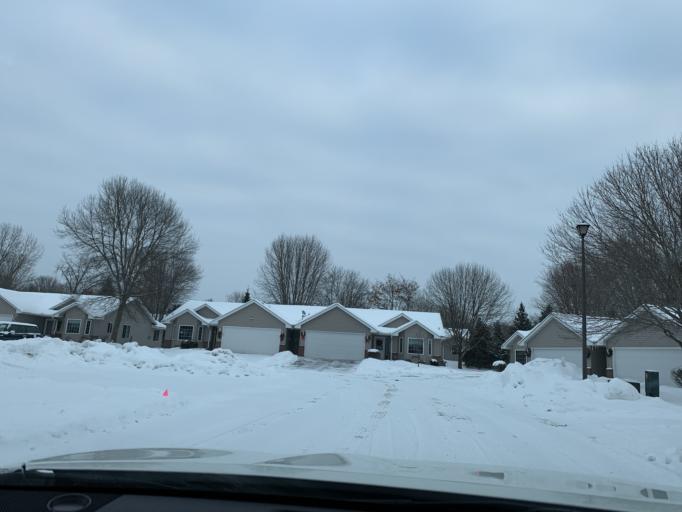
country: US
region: Minnesota
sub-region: Anoka County
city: Coon Rapids
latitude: 45.1610
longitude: -93.2911
